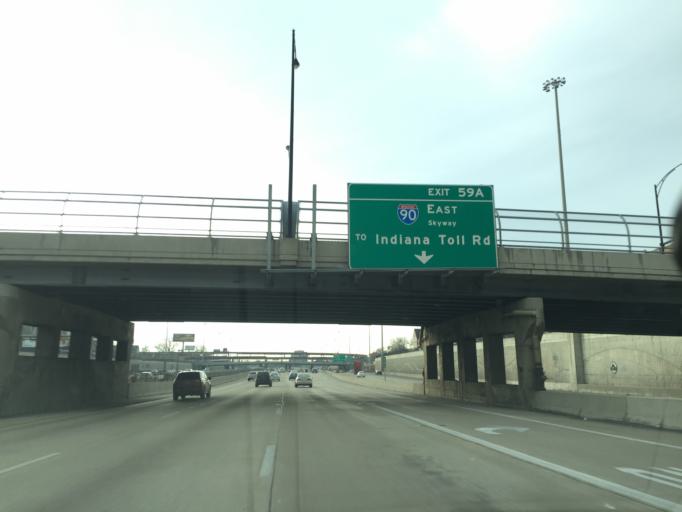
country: US
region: Illinois
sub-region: Cook County
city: Chicago
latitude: 41.7914
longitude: -87.6314
